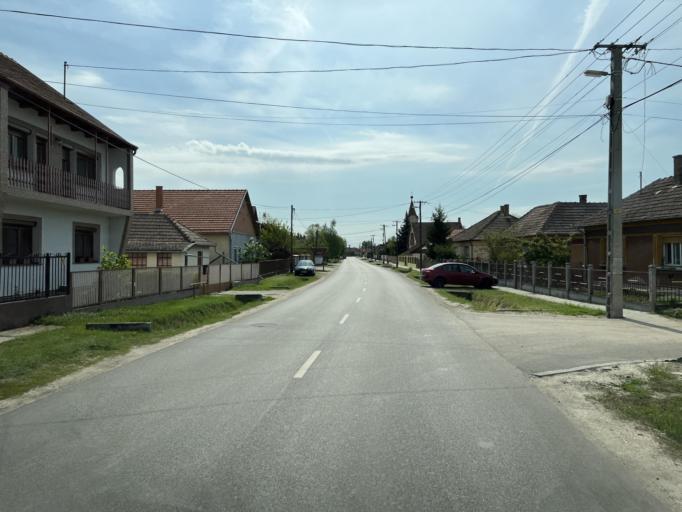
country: HU
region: Pest
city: Tapioszolos
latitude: 47.2939
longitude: 19.8365
